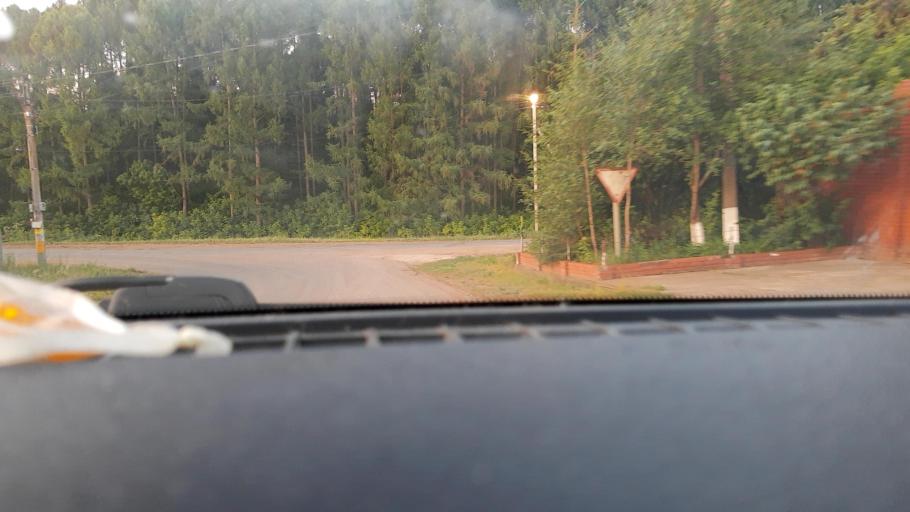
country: RU
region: Bashkortostan
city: Avdon
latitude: 54.6173
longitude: 55.6463
